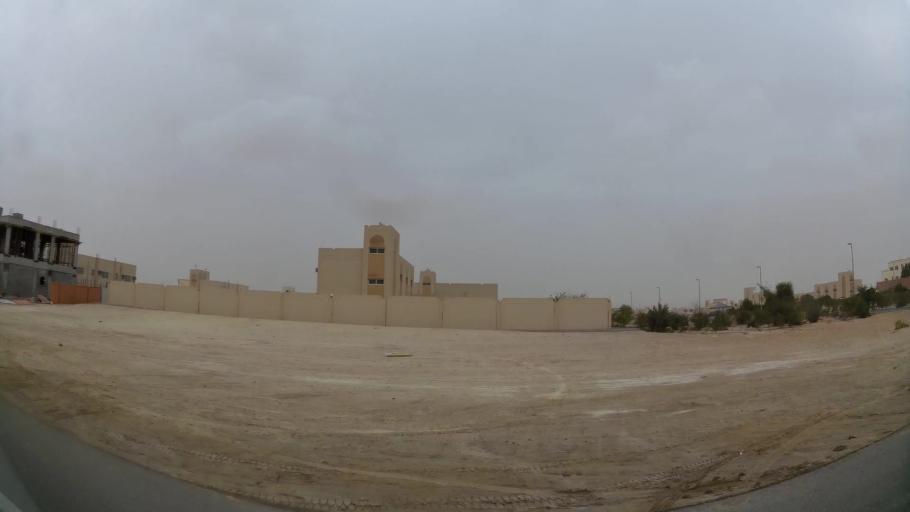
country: AE
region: Abu Dhabi
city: Abu Dhabi
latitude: 24.3765
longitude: 54.7061
